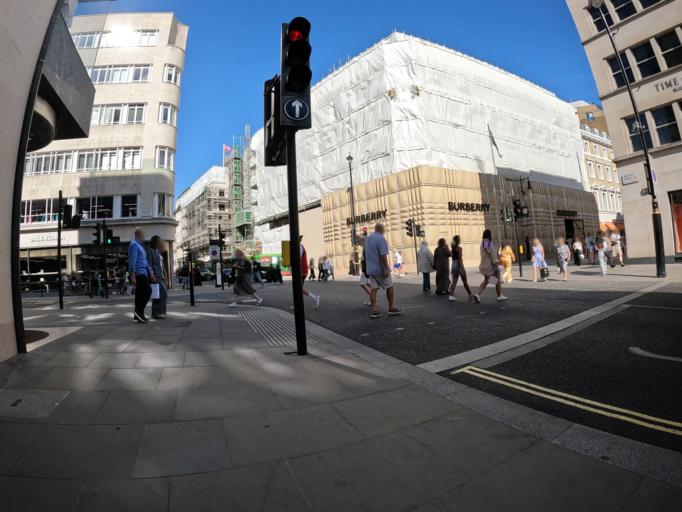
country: GB
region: England
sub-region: Greater London
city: London
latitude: 51.5112
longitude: -0.1436
